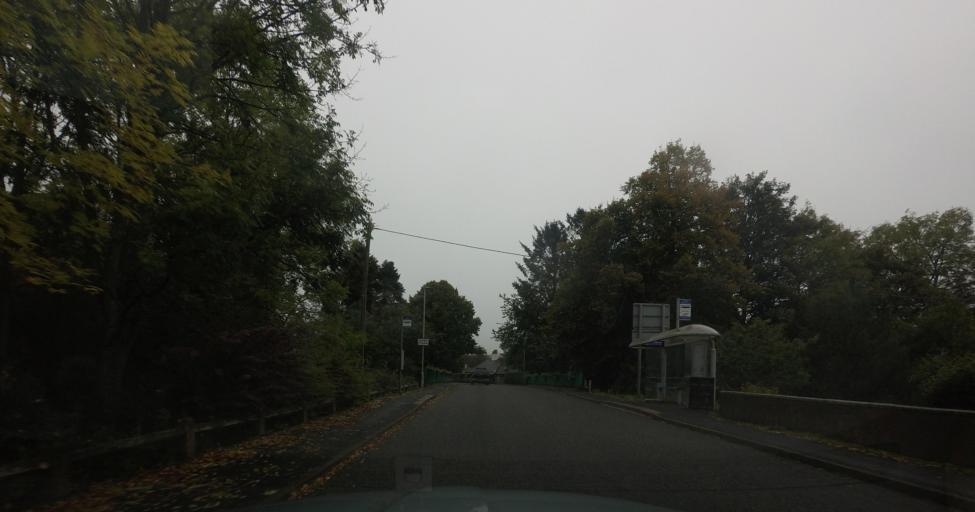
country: GB
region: Scotland
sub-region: Aberdeenshire
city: Oldmeldrum
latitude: 57.4284
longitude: -2.3958
